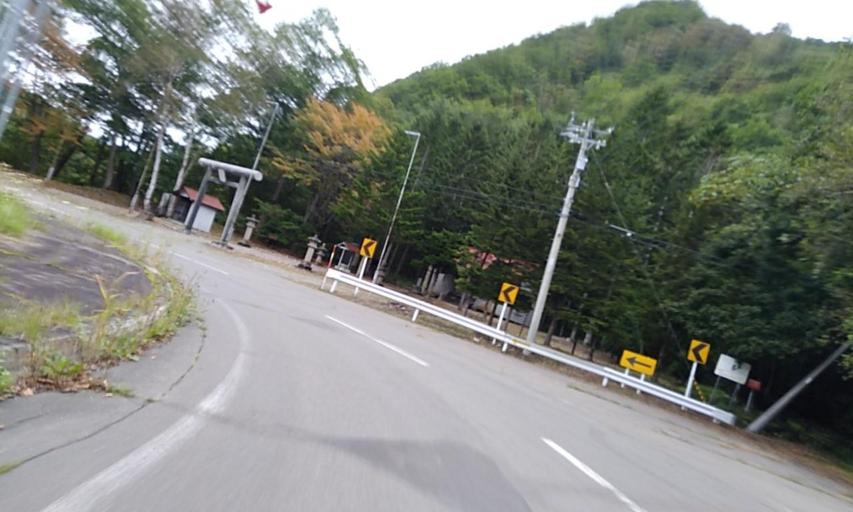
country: JP
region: Hokkaido
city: Obihiro
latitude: 42.6742
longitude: 143.0374
